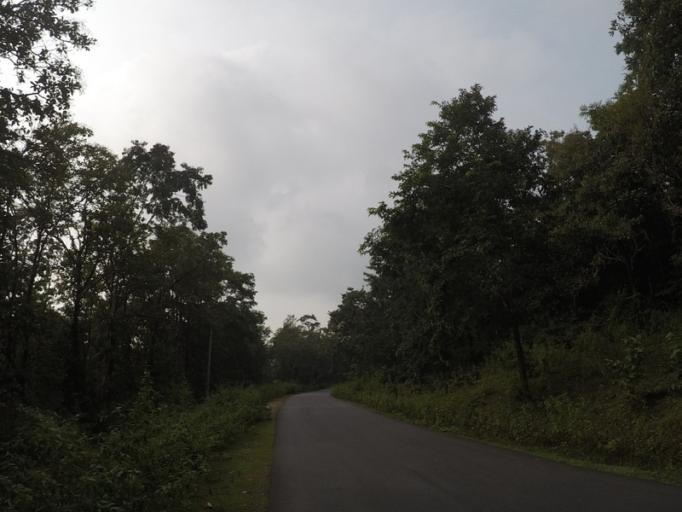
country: IN
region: Karnataka
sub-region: Chikmagalur
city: Mudigere
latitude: 13.2939
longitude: 75.4825
